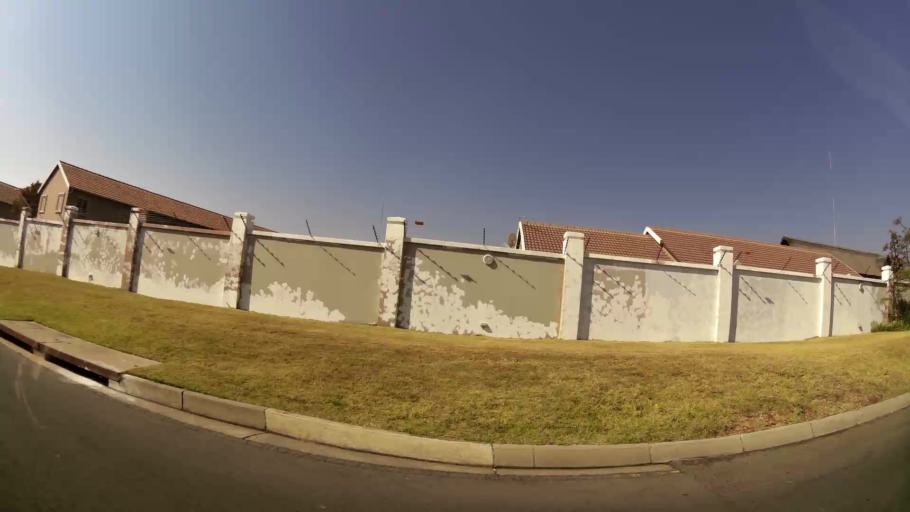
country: ZA
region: Gauteng
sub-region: City of Johannesburg Metropolitan Municipality
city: Modderfontein
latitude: -26.1153
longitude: 28.1631
